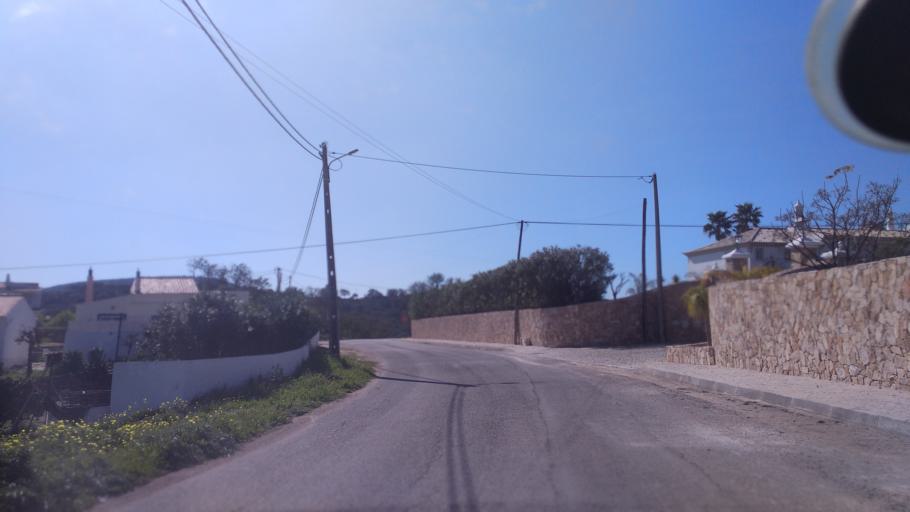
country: PT
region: Faro
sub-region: Faro
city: Santa Barbara de Nexe
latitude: 37.1119
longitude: -7.9334
